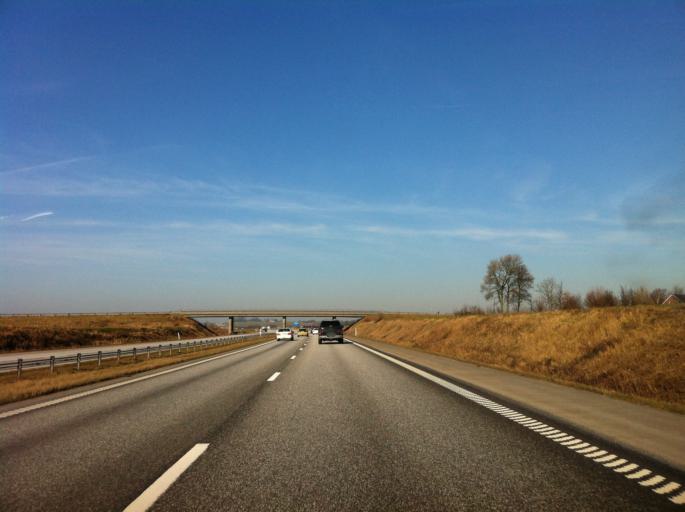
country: SE
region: Skane
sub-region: Landskrona
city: Landskrona
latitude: 55.9103
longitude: 12.8579
